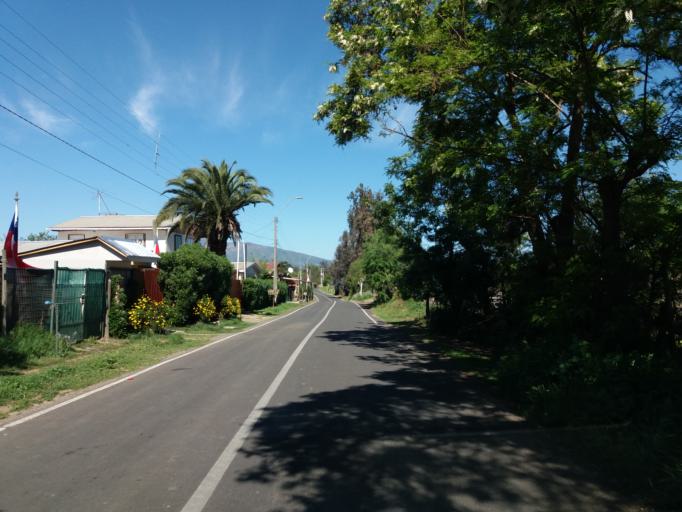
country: CL
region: Valparaiso
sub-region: Provincia de Marga Marga
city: Limache
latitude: -33.0054
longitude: -71.1889
